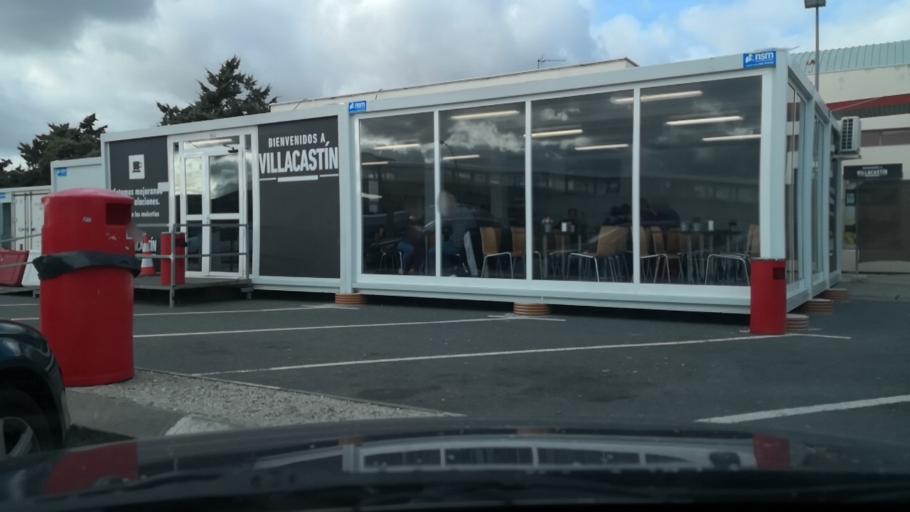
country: ES
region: Castille and Leon
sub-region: Provincia de Segovia
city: Villacastin
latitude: 40.7721
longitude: -4.3969
